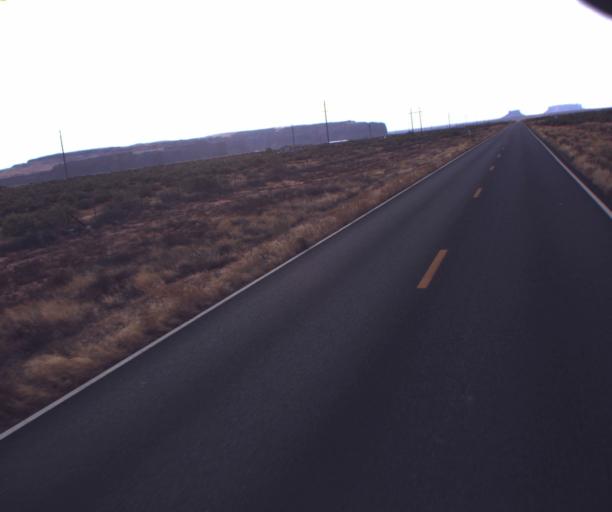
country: US
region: Arizona
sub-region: Apache County
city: Many Farms
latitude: 36.6647
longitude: -109.5971
